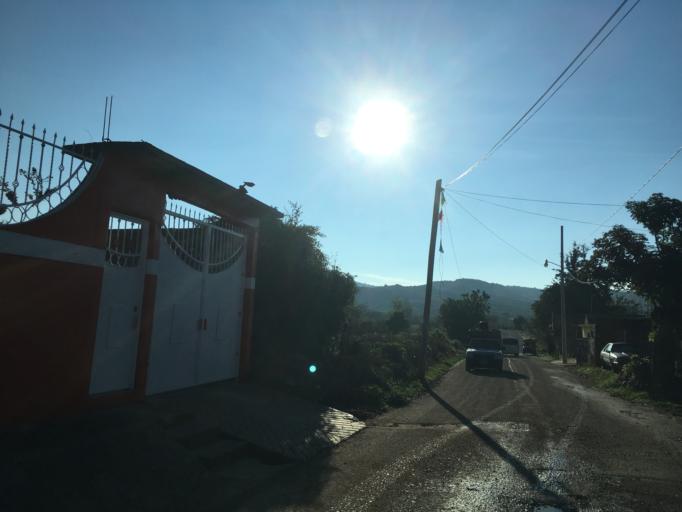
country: MX
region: Oaxaca
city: Santiago Tillo
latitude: 17.5329
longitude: -97.3418
